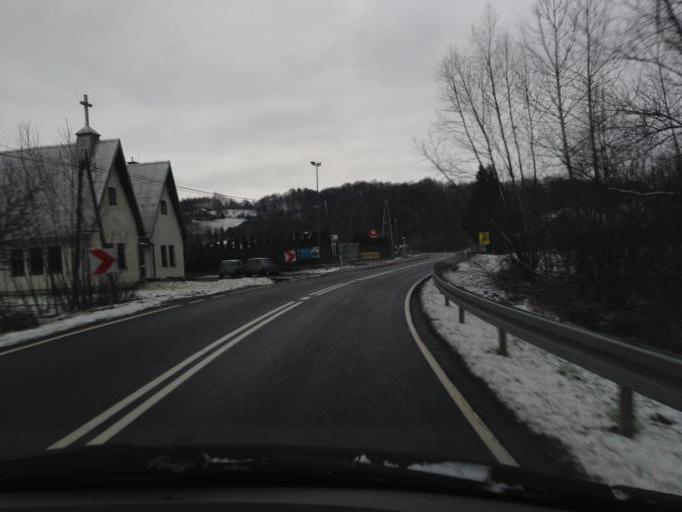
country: PL
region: Lesser Poland Voivodeship
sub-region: Powiat tarnowski
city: Rzepiennik Strzyzewski
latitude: 49.8084
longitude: 21.0318
